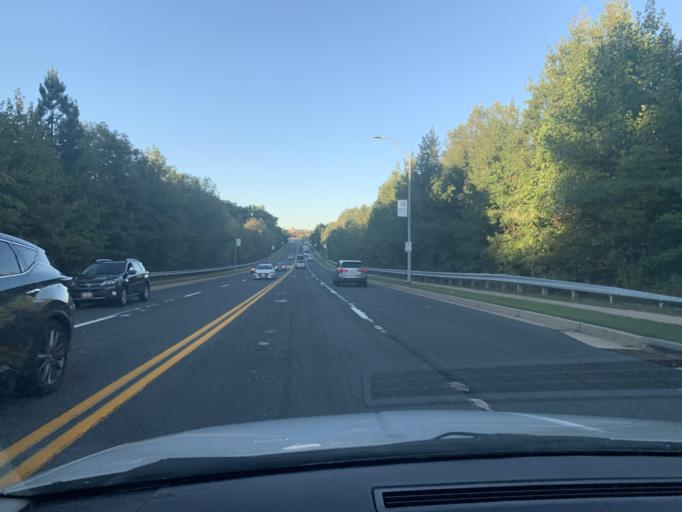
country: US
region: Maryland
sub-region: Baltimore County
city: Perry Hall
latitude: 39.3980
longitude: -76.4518
